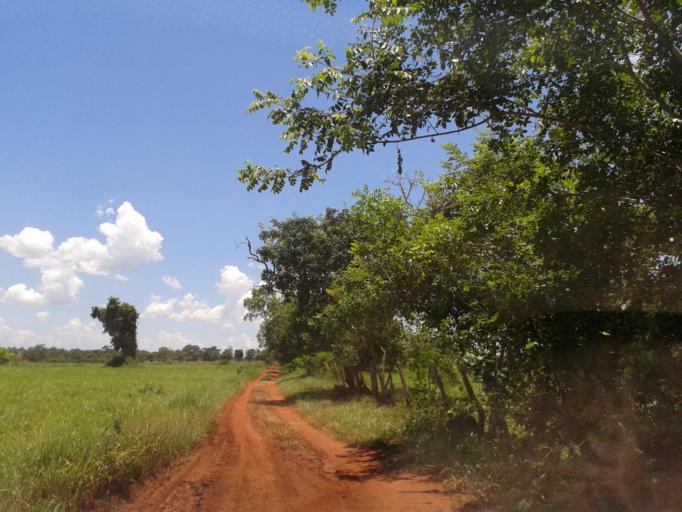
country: BR
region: Minas Gerais
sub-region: Santa Vitoria
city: Santa Vitoria
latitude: -19.1287
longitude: -50.5606
